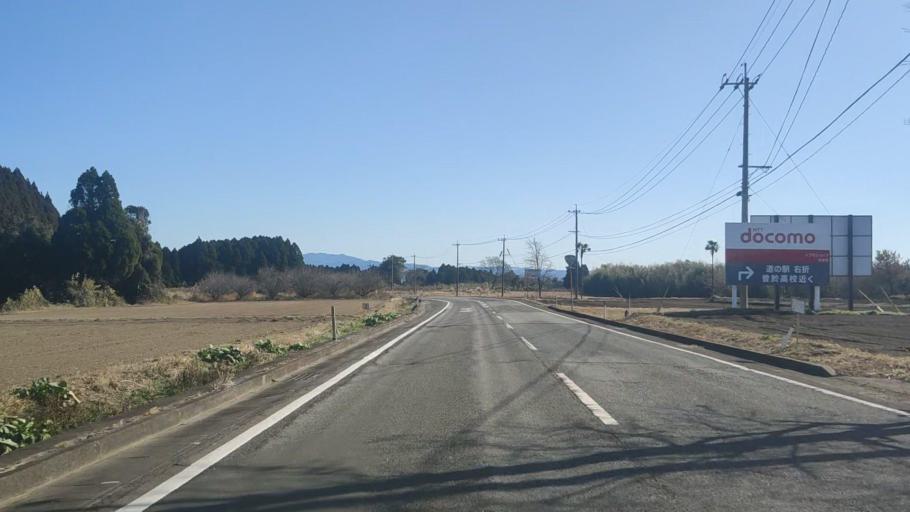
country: JP
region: Kagoshima
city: Sueyoshicho-ninokata
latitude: 31.6874
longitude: 130.9646
